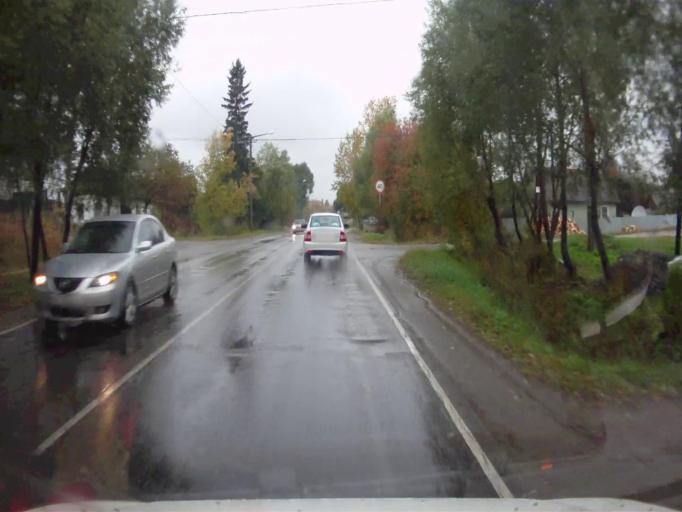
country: RU
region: Chelyabinsk
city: Kyshtym
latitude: 55.7209
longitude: 60.5399
